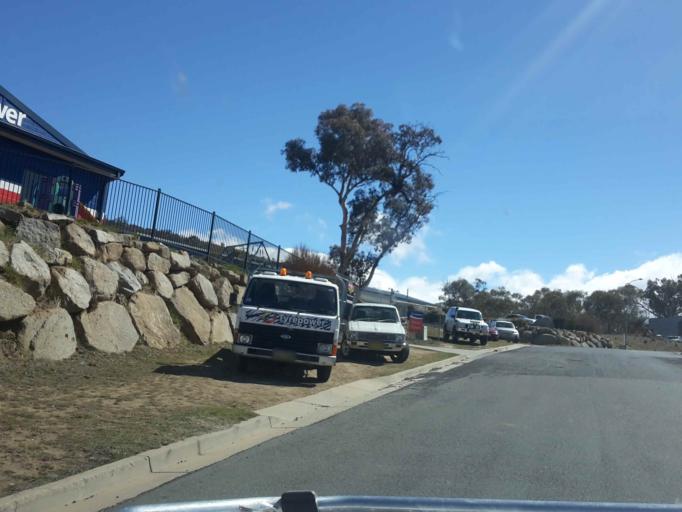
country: AU
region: New South Wales
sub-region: Snowy River
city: Jindabyne
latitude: -36.4373
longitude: 148.6001
